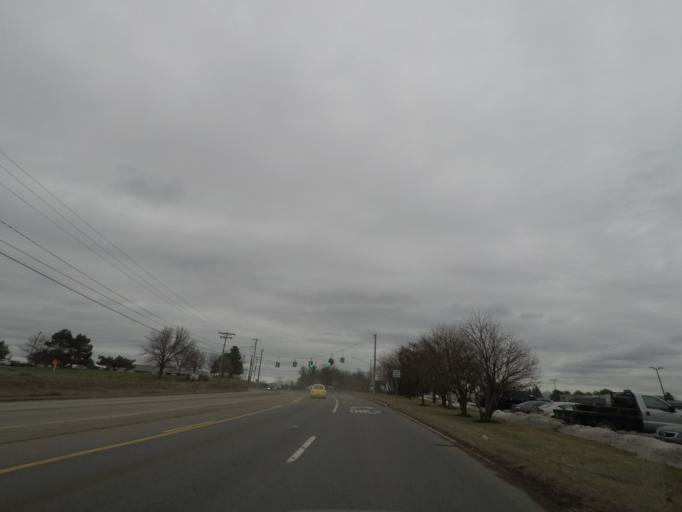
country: US
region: New York
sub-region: Albany County
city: Cohoes
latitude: 42.7625
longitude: -73.7508
